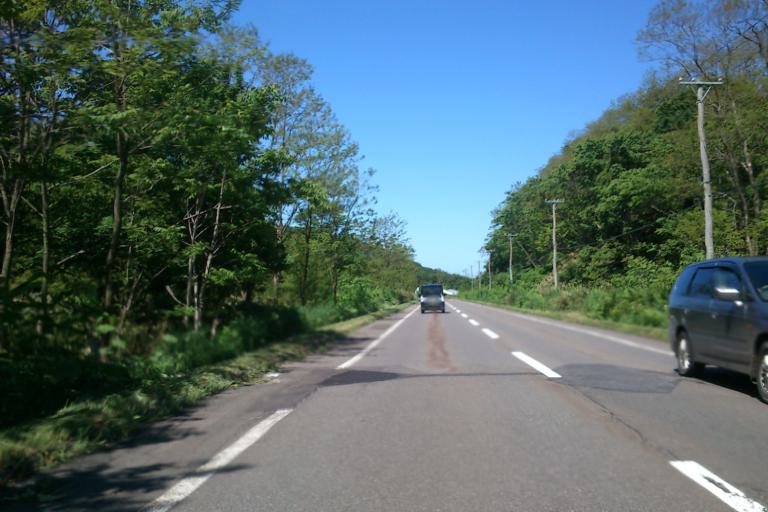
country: JP
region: Hokkaido
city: Ishikari
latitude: 43.5564
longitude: 141.3945
